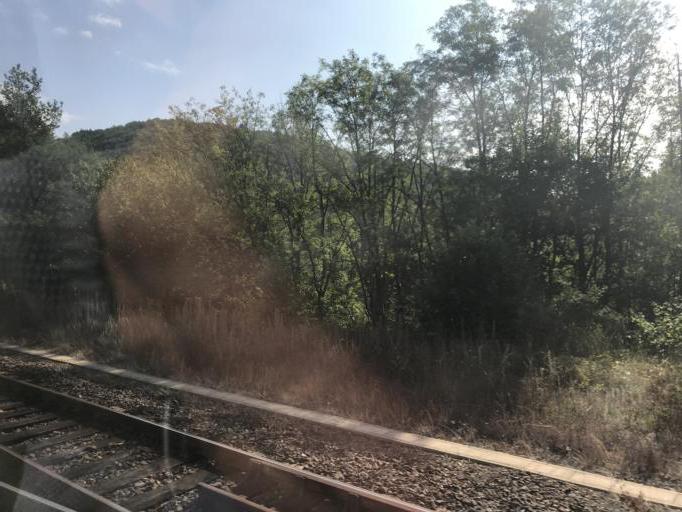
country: DE
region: Rheinland-Pfalz
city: Heimbach
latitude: 49.6148
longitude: 7.2291
